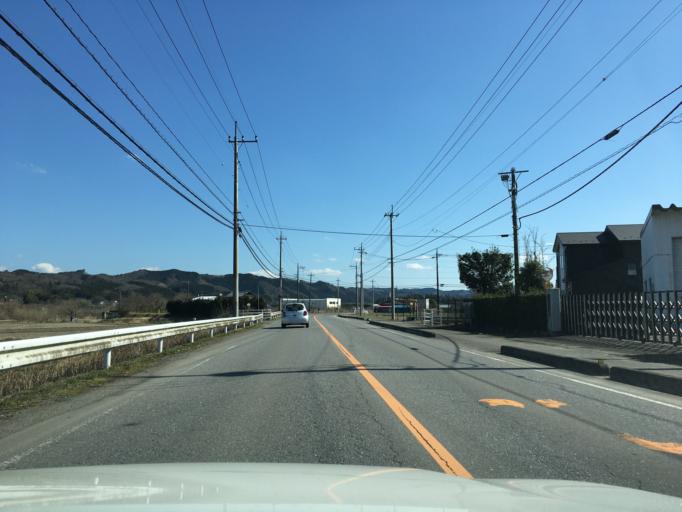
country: JP
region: Tochigi
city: Karasuyama
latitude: 36.7253
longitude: 140.1438
